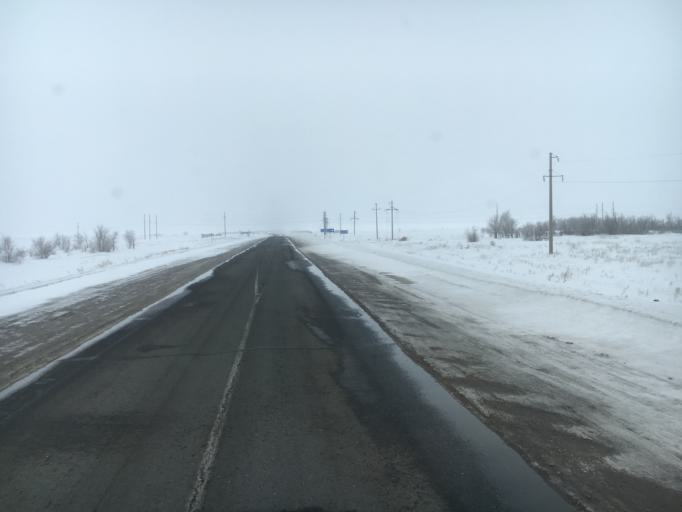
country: KZ
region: Batys Qazaqstan
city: Fedorovka
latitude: 50.7610
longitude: 51.9141
